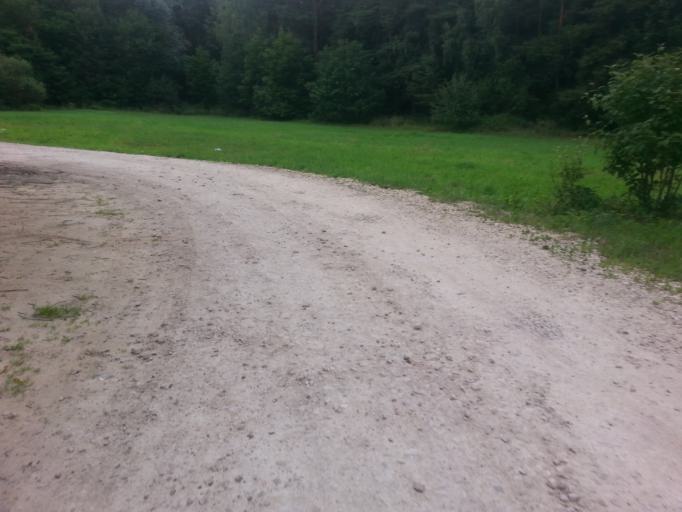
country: LV
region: Stopini
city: Ulbroka
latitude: 56.9682
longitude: 24.2472
